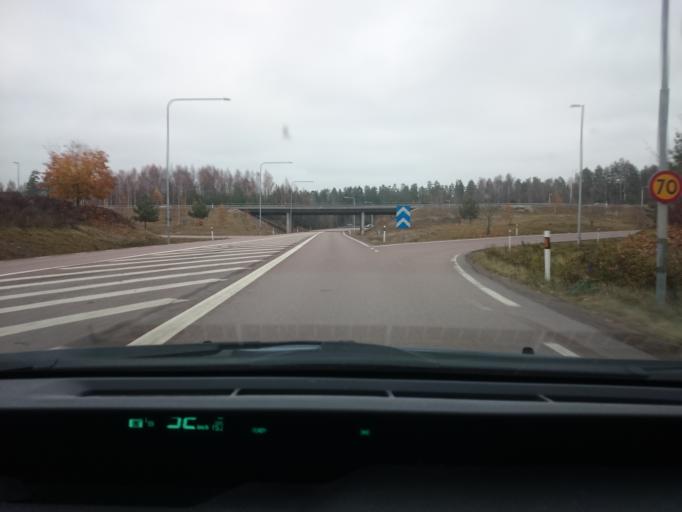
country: SE
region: Dalarna
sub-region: Avesta Kommun
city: Avesta
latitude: 60.1512
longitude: 16.2024
